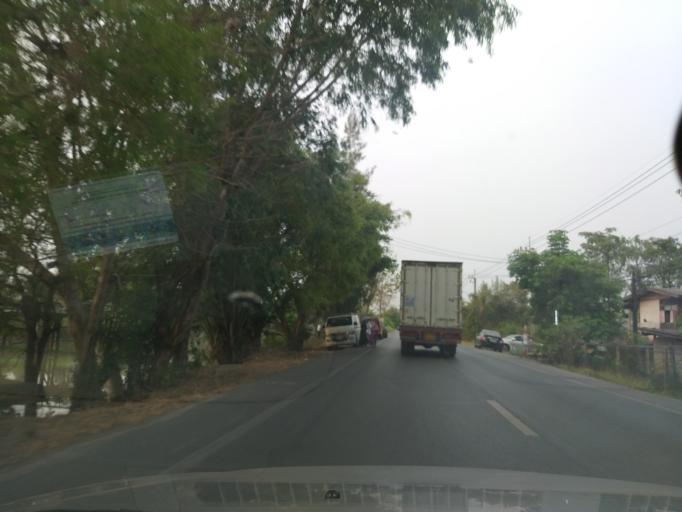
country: TH
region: Bangkok
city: Nong Chok
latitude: 13.8824
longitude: 100.8856
